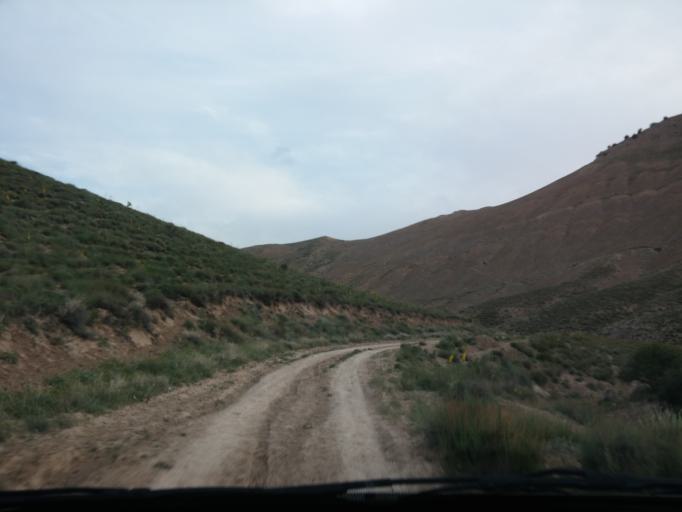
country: IR
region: Semnan
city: Istgah-e Rah Ahan-e Garmsar
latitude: 35.4852
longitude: 52.2938
